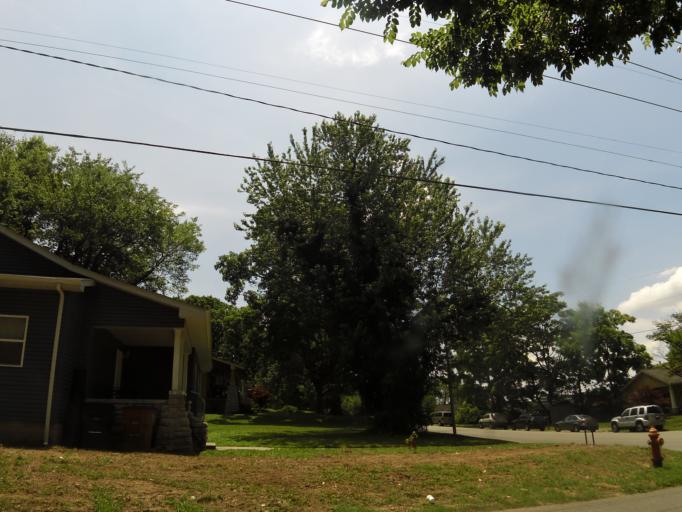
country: US
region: Tennessee
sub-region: Davidson County
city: Nashville
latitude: 36.1854
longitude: -86.7459
